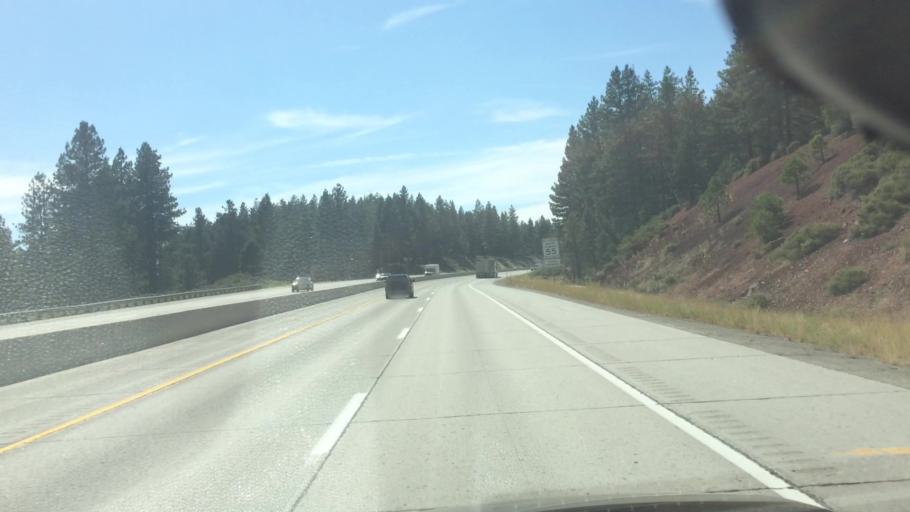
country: US
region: California
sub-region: Nevada County
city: Truckee
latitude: 39.3730
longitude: -120.0606
